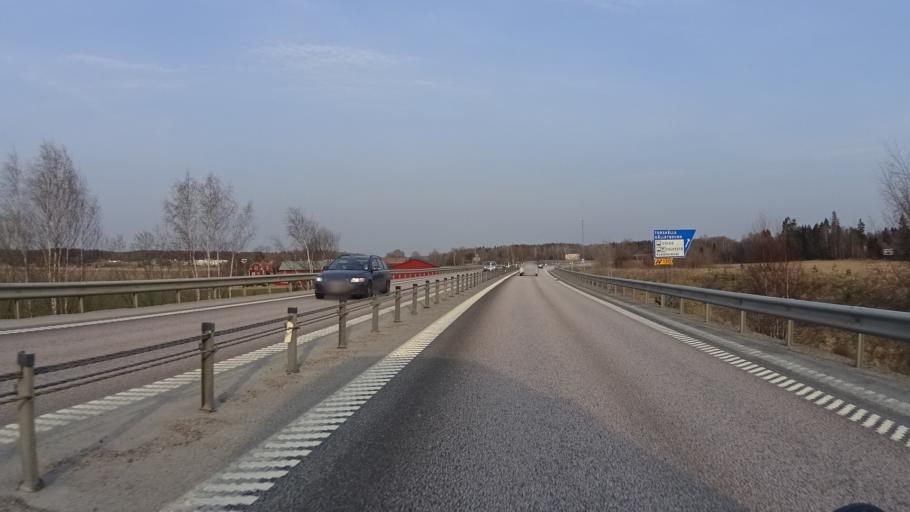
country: SE
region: Soedermanland
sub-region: Eskilstuna Kommun
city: Hallbybrunn
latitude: 59.4073
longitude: 16.4116
